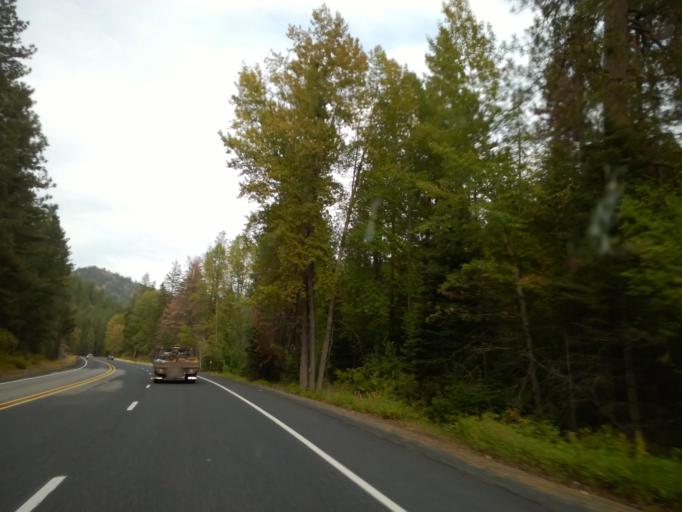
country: US
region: Washington
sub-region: Chelan County
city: Leavenworth
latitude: 47.3935
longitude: -120.6380
